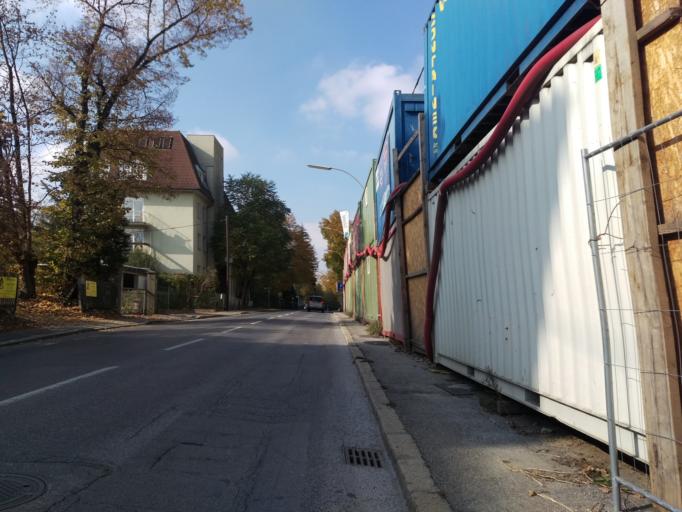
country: AT
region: Styria
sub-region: Graz Stadt
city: Graz
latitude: 47.0796
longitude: 15.4635
